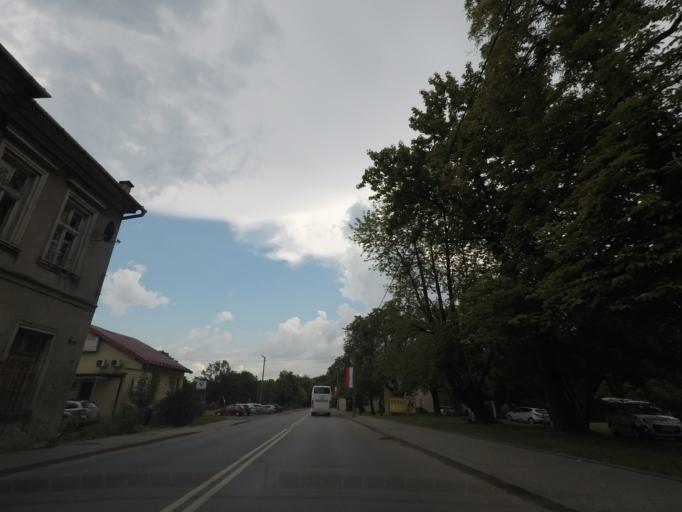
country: PL
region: Lesser Poland Voivodeship
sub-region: Powiat wielicki
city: Wieliczka
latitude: 49.9893
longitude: 20.0479
